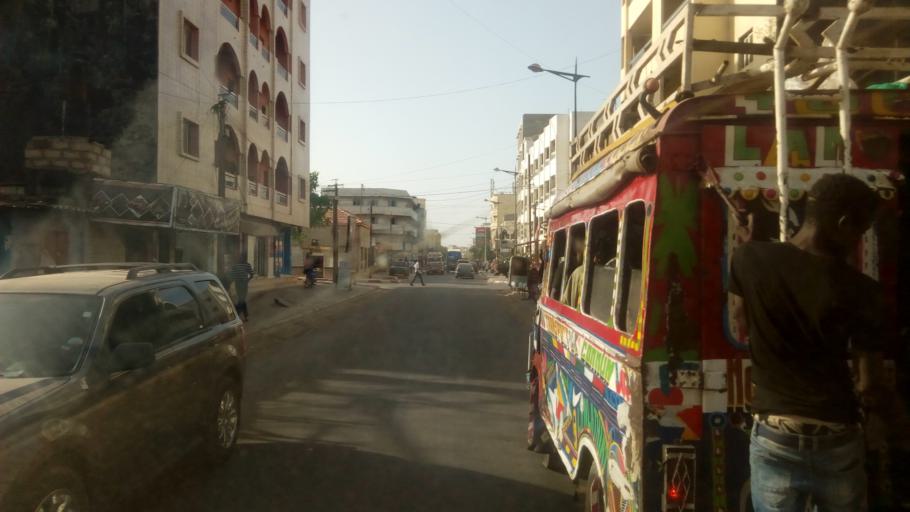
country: SN
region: Dakar
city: Dakar
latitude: 14.6843
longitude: -17.4484
